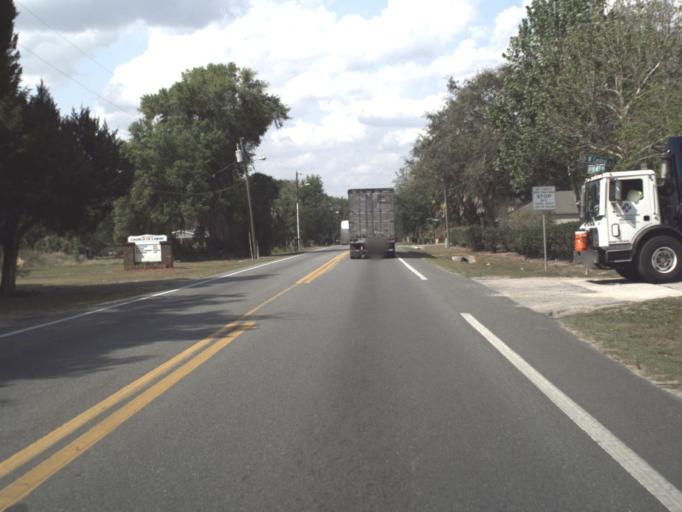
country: US
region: Florida
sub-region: Lake County
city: Groveland
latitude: 28.5643
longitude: -81.8555
